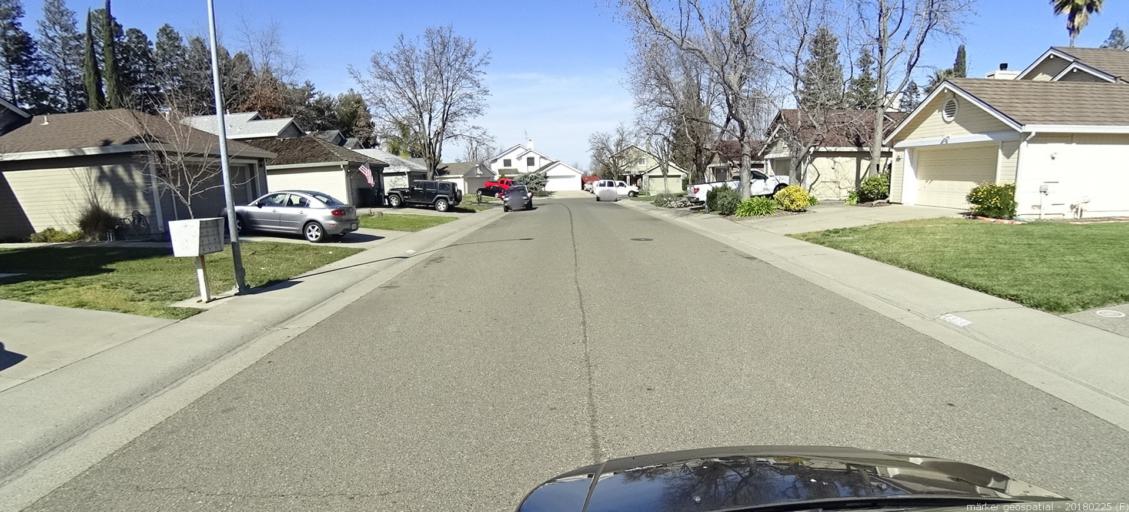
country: US
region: California
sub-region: Sacramento County
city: Antelope
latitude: 38.7256
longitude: -121.3640
